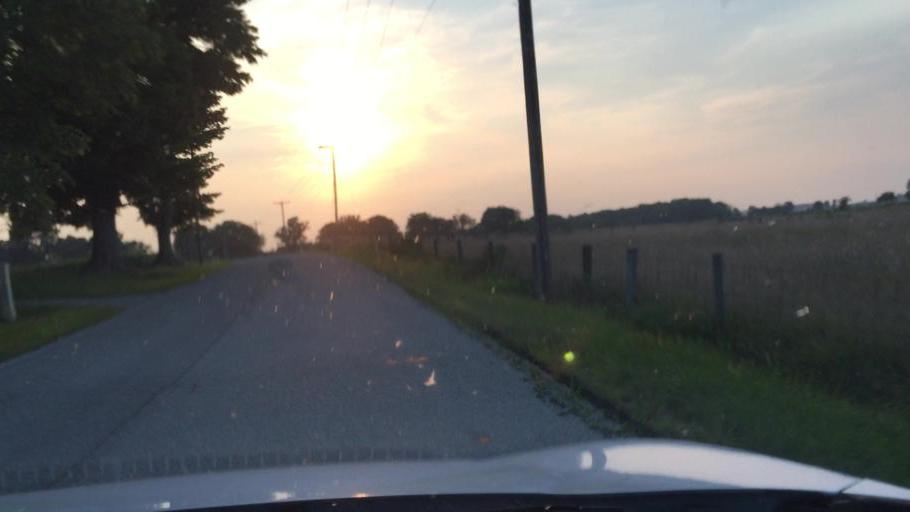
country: US
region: Ohio
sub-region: Madison County
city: Choctaw Lake
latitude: 39.9474
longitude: -83.5513
